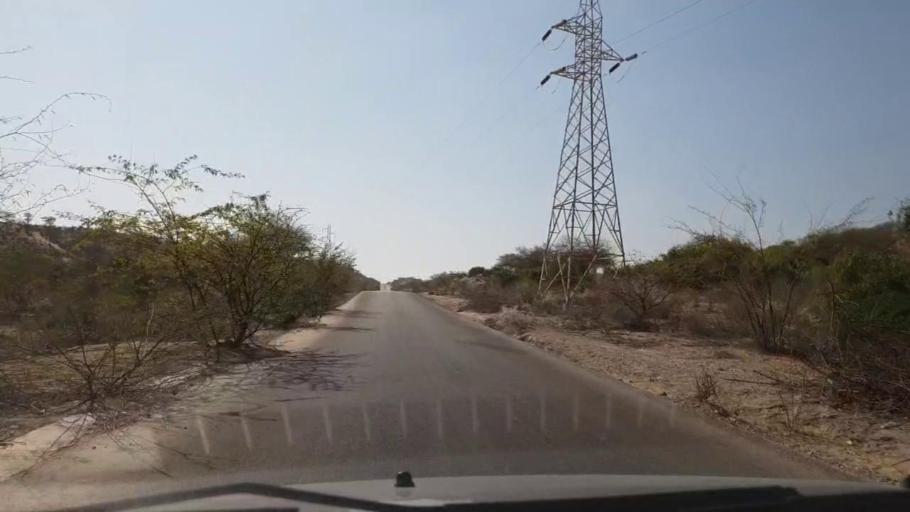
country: PK
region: Sindh
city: Mithi
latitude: 24.6322
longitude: 69.7399
